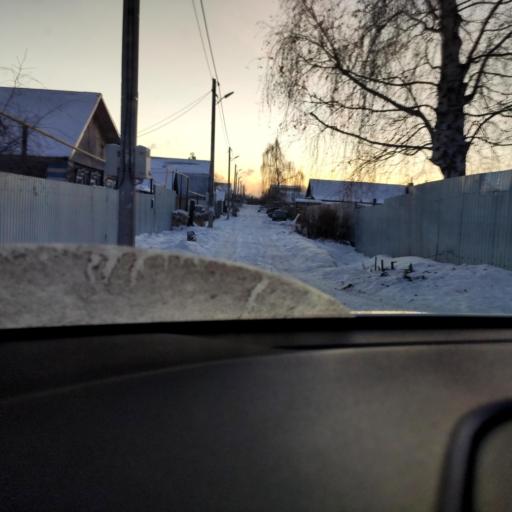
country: RU
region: Tatarstan
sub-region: Gorod Kazan'
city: Kazan
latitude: 55.7382
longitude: 49.0934
